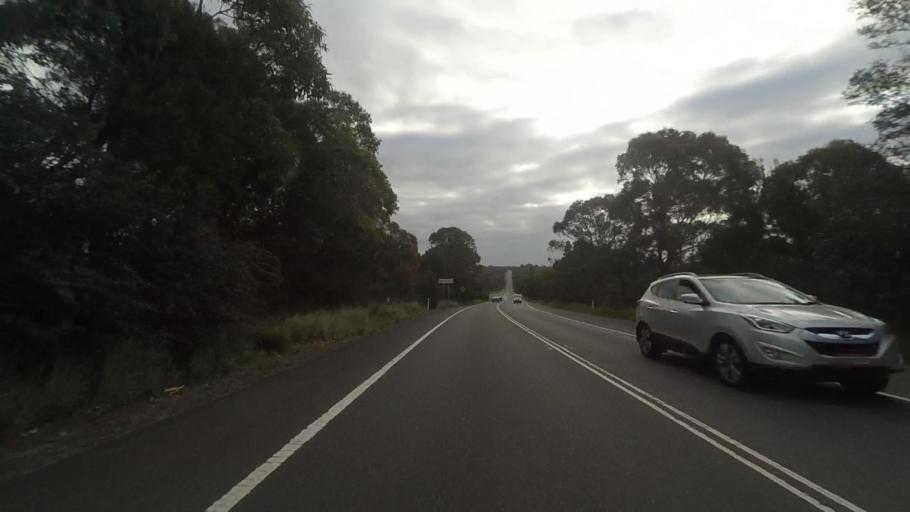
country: AU
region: New South Wales
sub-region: Sutherland Shire
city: Engadine
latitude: -34.0451
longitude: 150.9914
